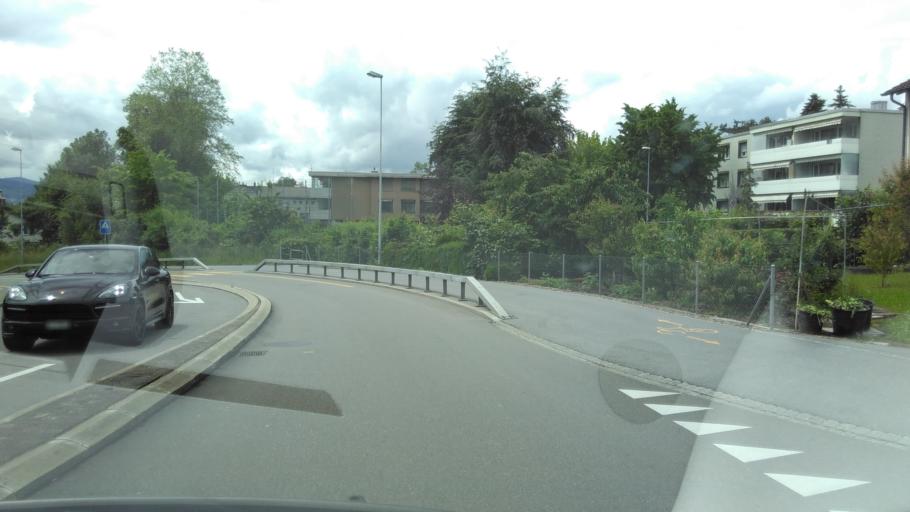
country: CH
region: Saint Gallen
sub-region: Wahlkreis See-Gaster
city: Rapperswil
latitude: 47.2390
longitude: 8.8232
